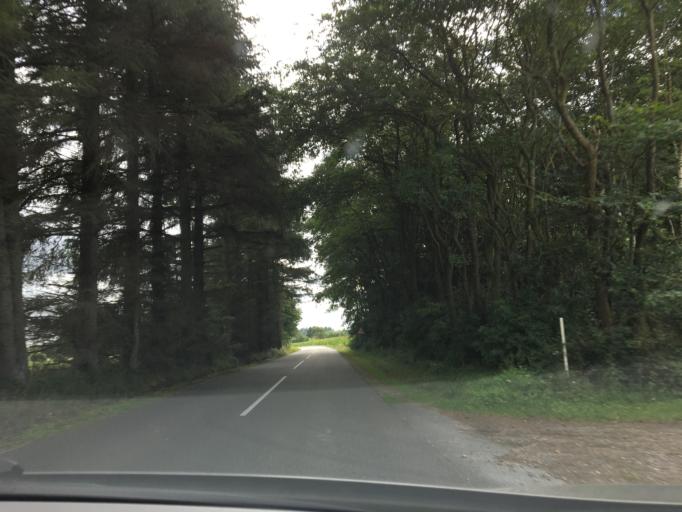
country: DK
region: South Denmark
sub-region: Varde Kommune
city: Oksbol
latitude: 55.7464
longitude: 8.2657
